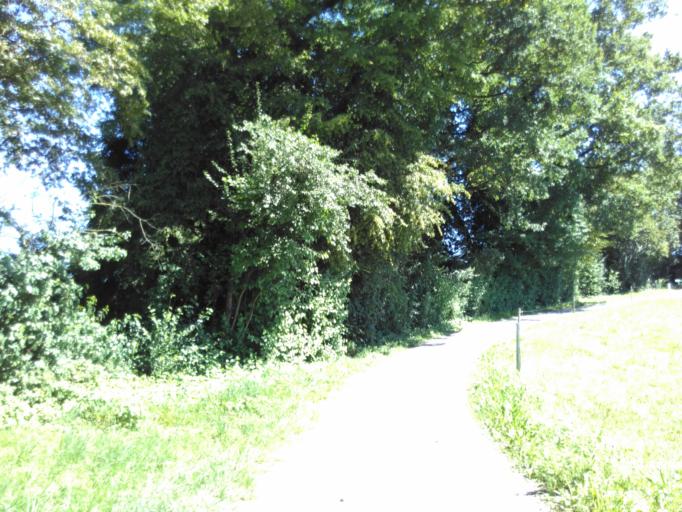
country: CH
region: Zurich
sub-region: Bezirk Hinwil
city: Rueti
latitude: 47.2538
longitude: 8.8516
